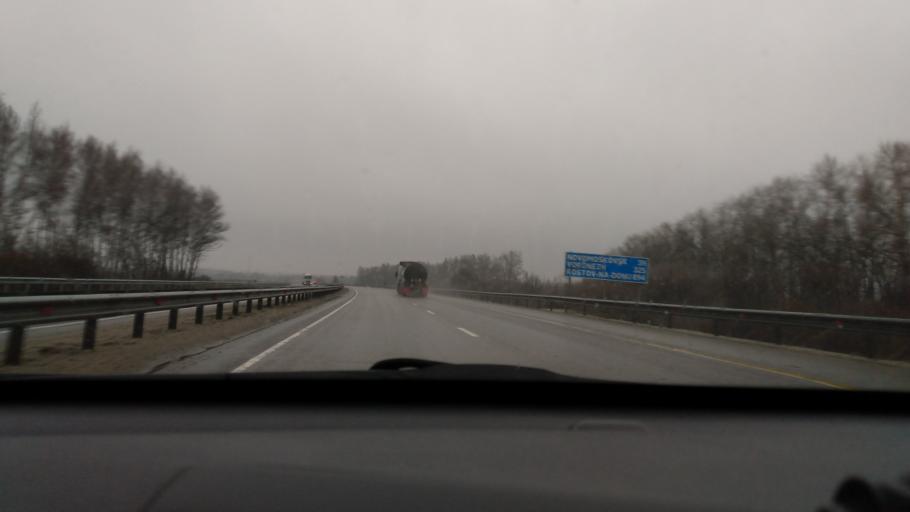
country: RU
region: Tula
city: Gritsovskiy
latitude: 54.1565
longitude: 38.0736
